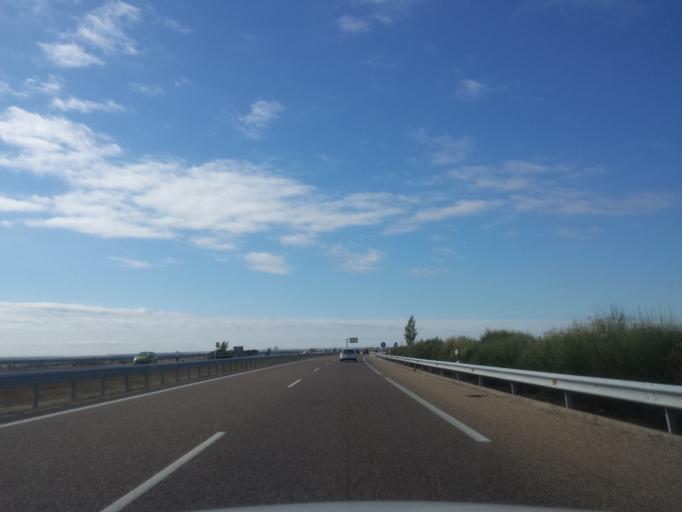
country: ES
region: Castille and Leon
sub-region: Provincia de Leon
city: Toral de los Guzmanes
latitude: 42.2454
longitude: -5.5919
